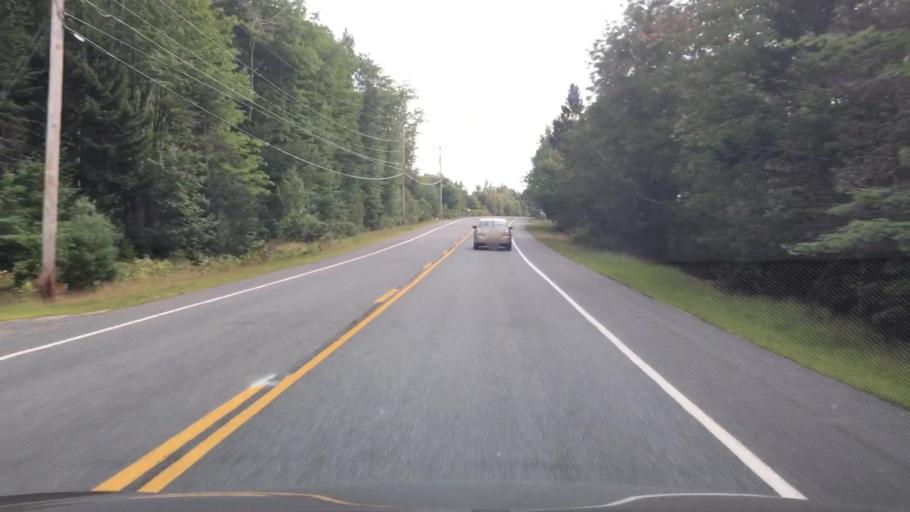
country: US
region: Maine
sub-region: Hancock County
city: Surry
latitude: 44.4452
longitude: -68.5629
